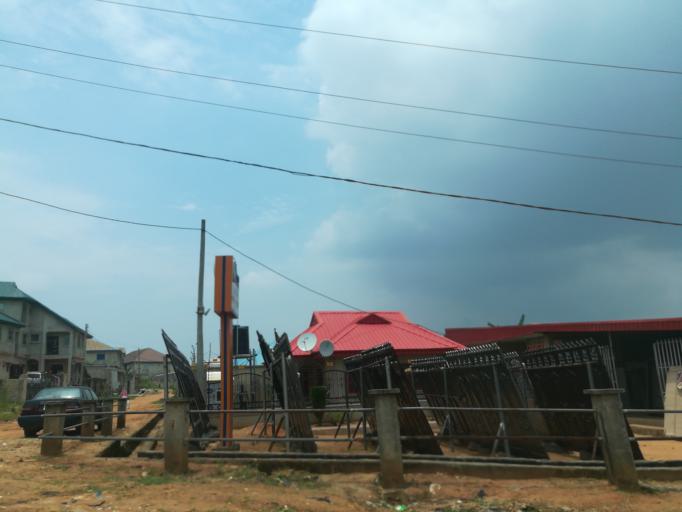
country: NG
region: Lagos
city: Ikorodu
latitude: 6.6232
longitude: 3.5555
